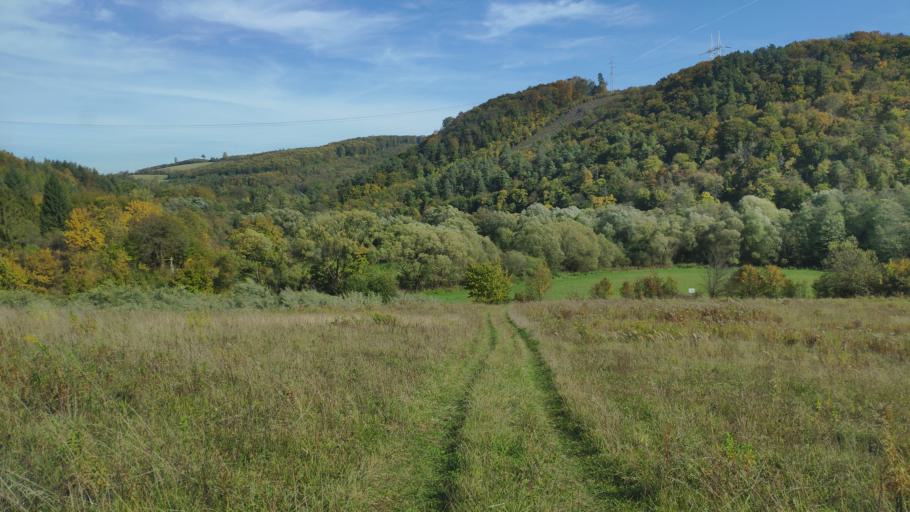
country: SK
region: Presovsky
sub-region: Okres Presov
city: Presov
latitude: 48.8959
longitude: 21.2024
